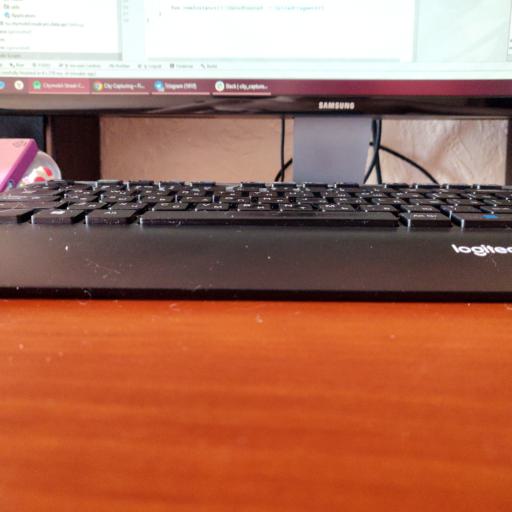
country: FI
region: Varsinais-Suomi
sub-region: Salo
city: Somero
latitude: 60.6230
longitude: 23.4601
